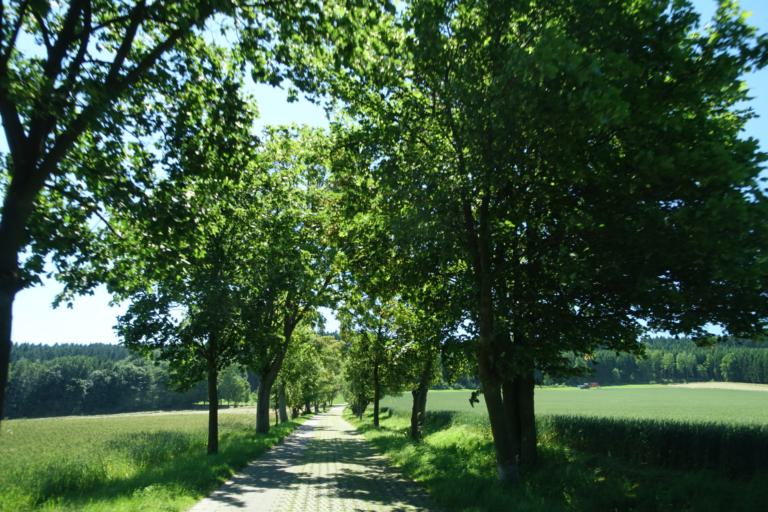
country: DE
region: Saxony
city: Bornichen
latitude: 50.7600
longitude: 13.1486
